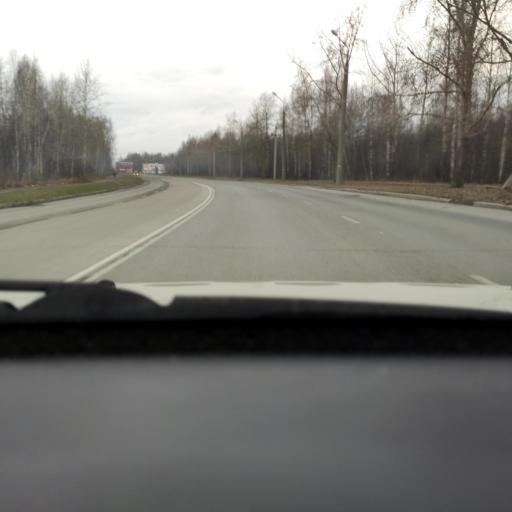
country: RU
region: Perm
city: Polazna
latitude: 58.1291
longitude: 56.4065
